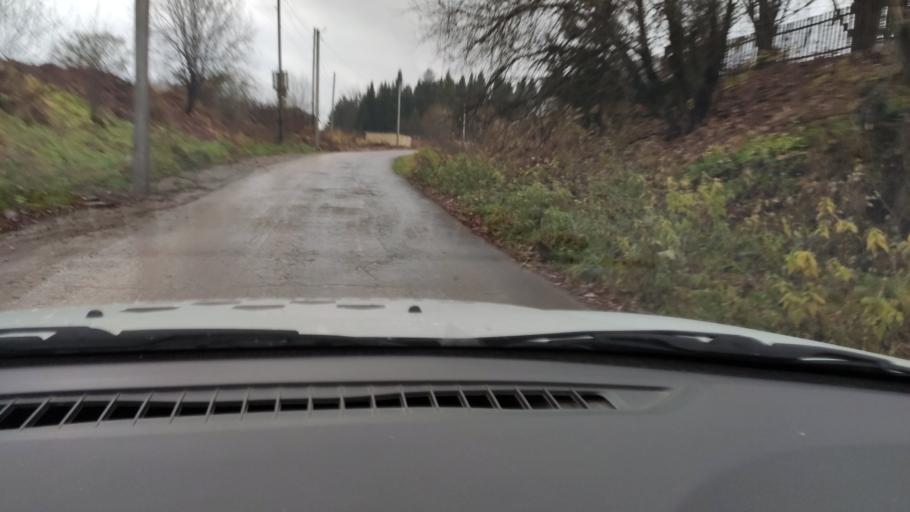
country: RU
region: Perm
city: Sylva
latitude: 58.0408
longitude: 56.7492
